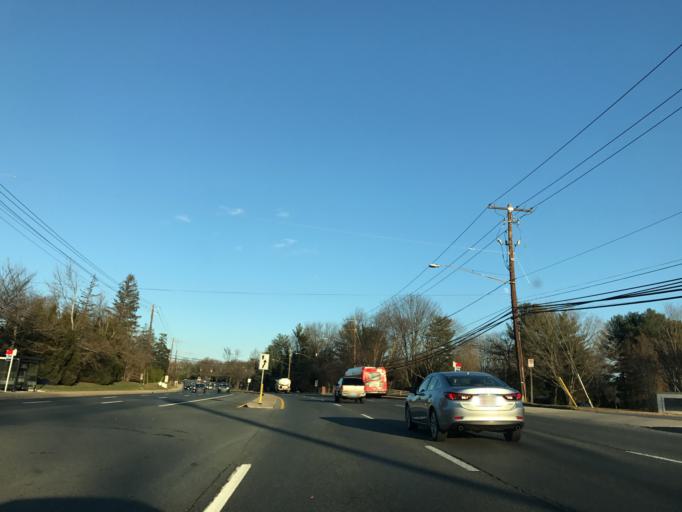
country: US
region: Maryland
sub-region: Montgomery County
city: Colesville
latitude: 39.0664
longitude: -77.0200
